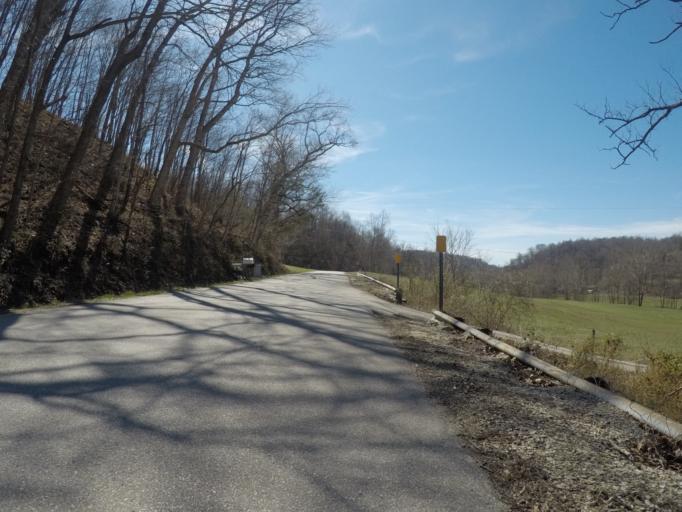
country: US
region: Ohio
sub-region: Lawrence County
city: South Point
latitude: 38.4717
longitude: -82.5662
